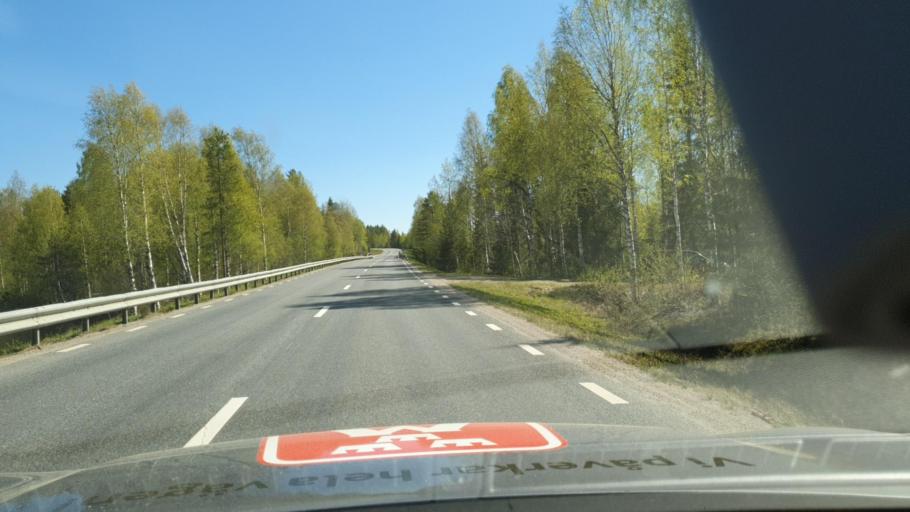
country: SE
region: Vaesternorrland
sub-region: OErnskoeldsviks Kommun
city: Ornskoldsvik
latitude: 63.7024
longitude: 18.5044
